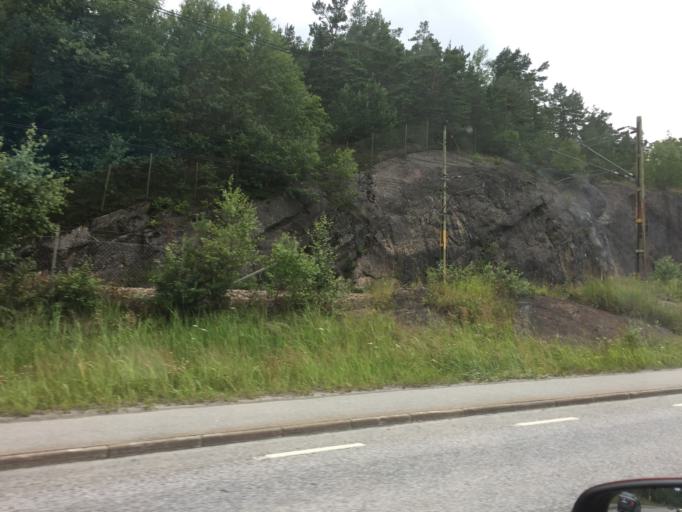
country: SE
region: Stockholm
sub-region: Botkyrka Kommun
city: Tullinge
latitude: 59.2005
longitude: 17.8764
